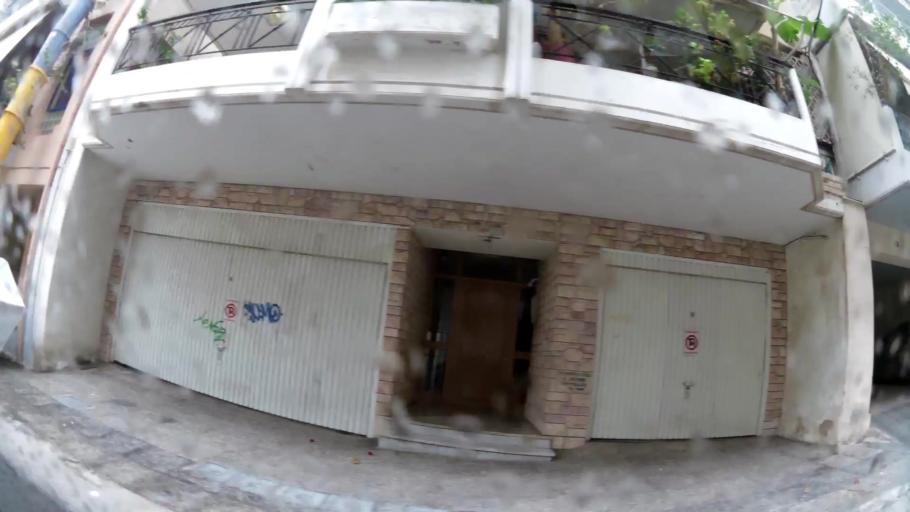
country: GR
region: Attica
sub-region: Nomos Attikis
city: Piraeus
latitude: 37.9325
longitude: 23.6343
